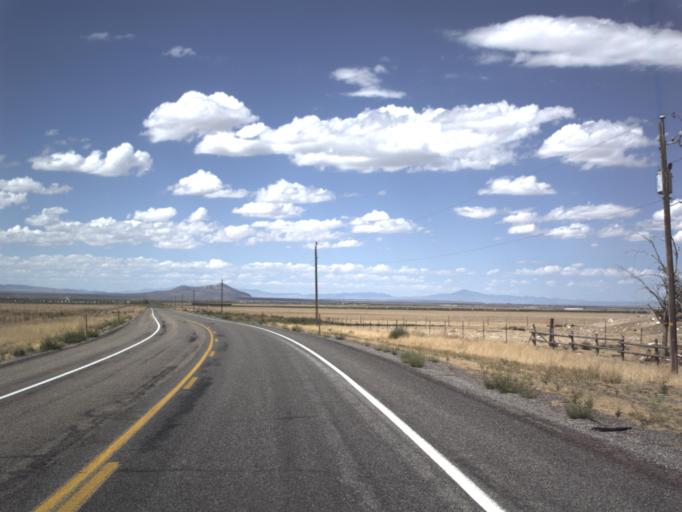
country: US
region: Utah
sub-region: Millard County
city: Fillmore
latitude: 39.1175
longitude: -112.3145
